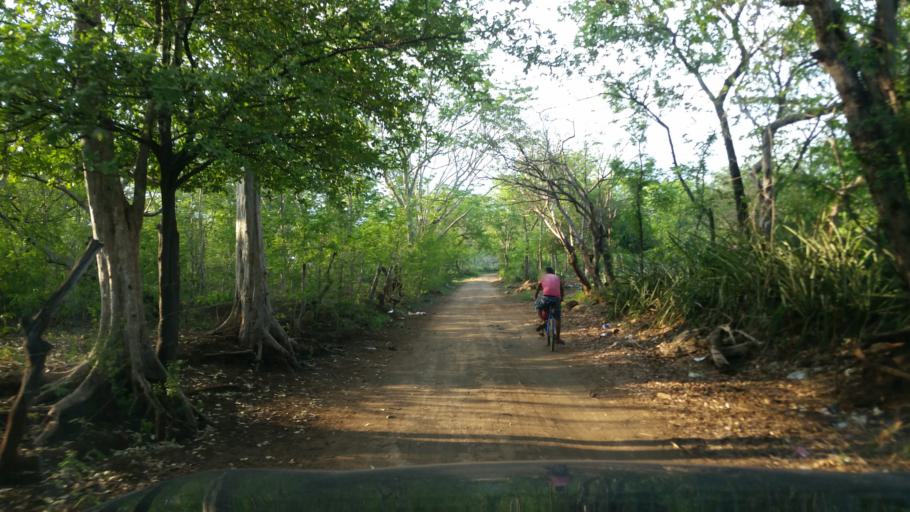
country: NI
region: Managua
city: Masachapa
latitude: 11.7822
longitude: -86.4736
